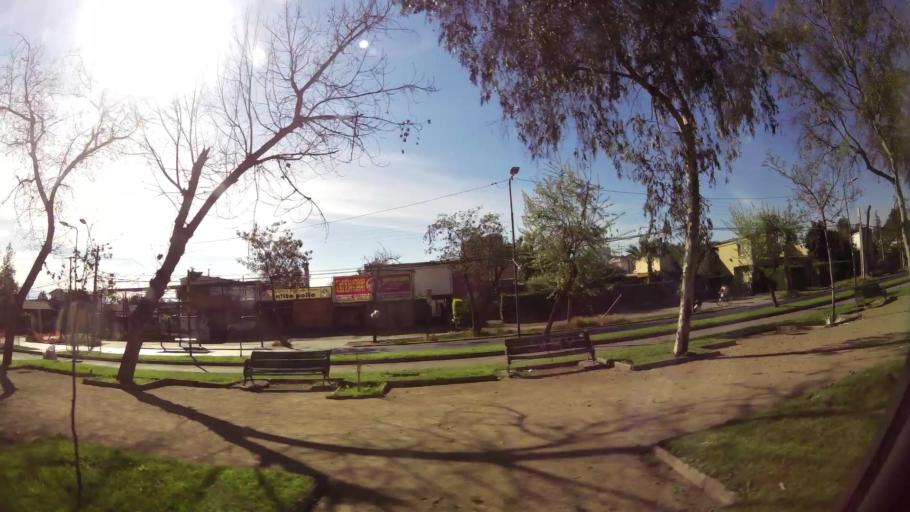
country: CL
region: Santiago Metropolitan
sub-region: Provincia de Santiago
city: Lo Prado
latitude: -33.4637
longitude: -70.7021
